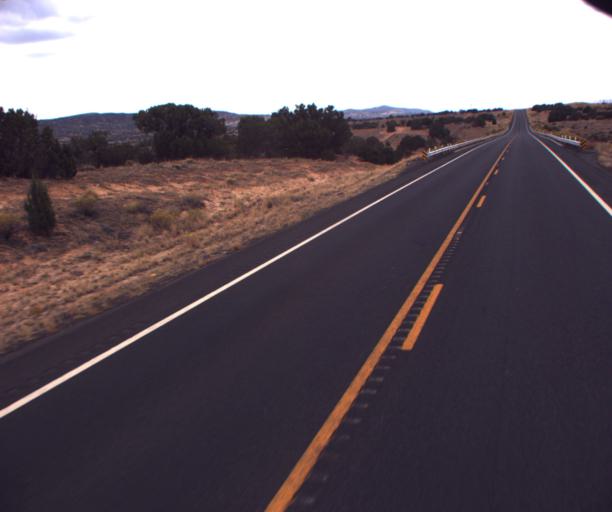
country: US
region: Arizona
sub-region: Coconino County
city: Kaibito
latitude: 36.4461
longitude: -110.7280
